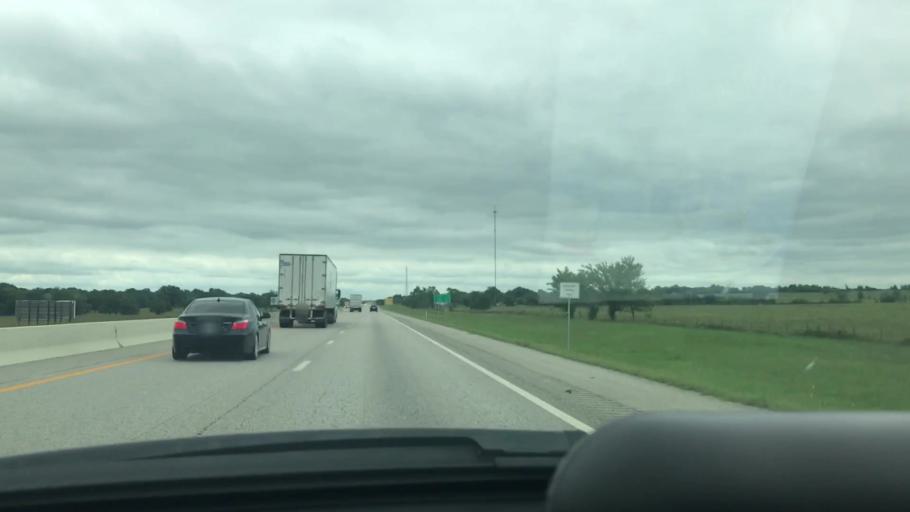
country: US
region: Oklahoma
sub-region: Craig County
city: Vinita
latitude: 36.5716
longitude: -95.2073
